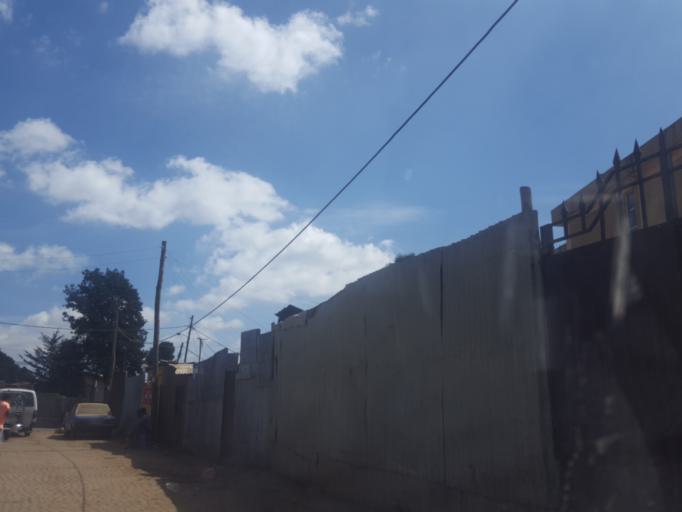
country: ET
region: Adis Abeba
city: Addis Ababa
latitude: 9.0501
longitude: 38.7307
